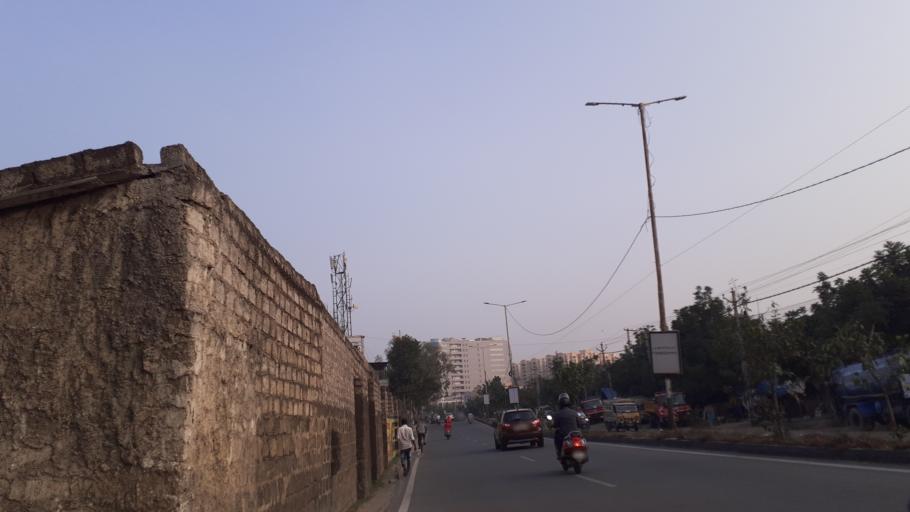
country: IN
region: Telangana
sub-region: Medak
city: Serilingampalle
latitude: 17.4891
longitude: 78.3547
